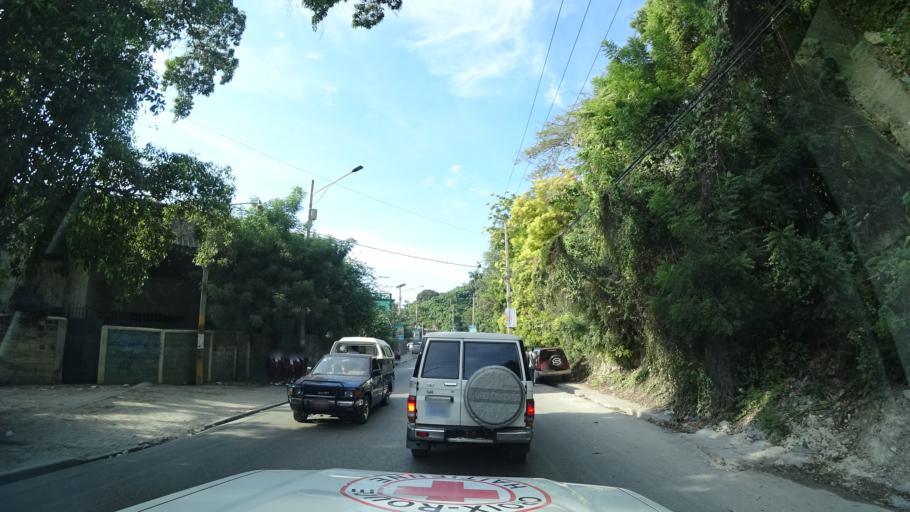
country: HT
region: Ouest
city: Delmas 73
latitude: 18.5359
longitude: -72.3112
